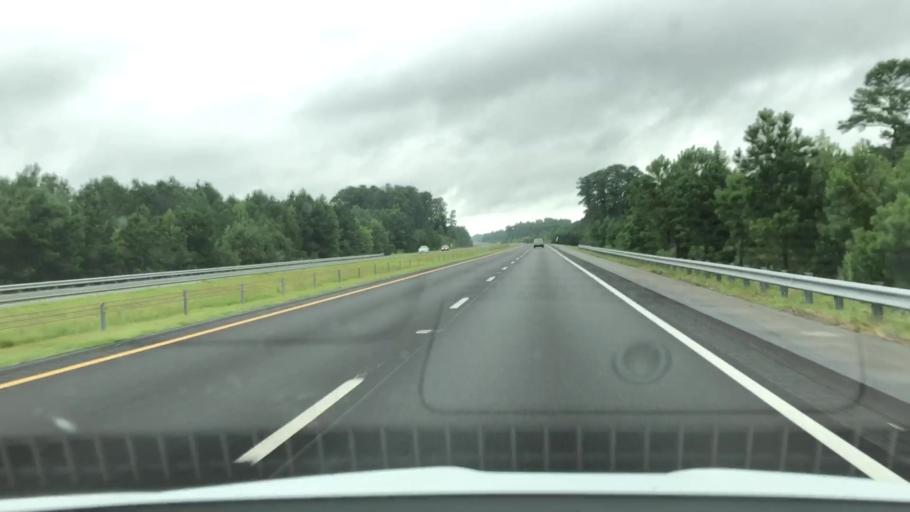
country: US
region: North Carolina
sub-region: Wayne County
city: Goldsboro
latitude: 35.4470
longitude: -77.9843
